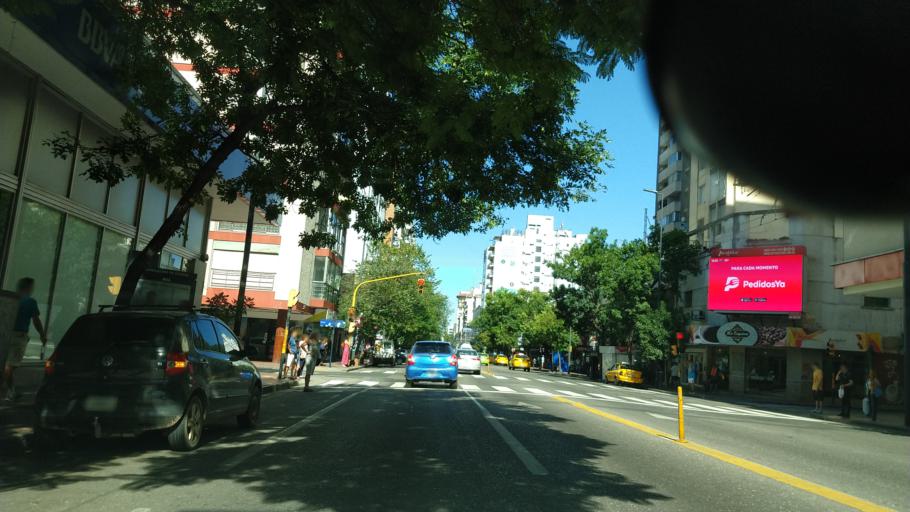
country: AR
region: Cordoba
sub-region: Departamento de Capital
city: Cordoba
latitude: -31.4118
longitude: -64.1887
